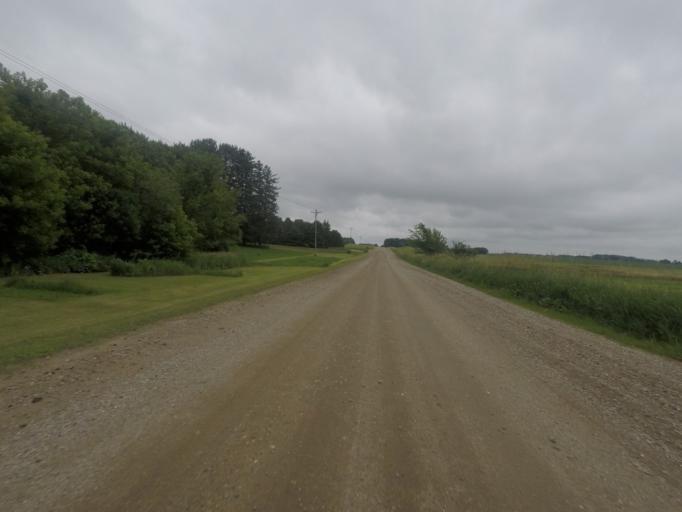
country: US
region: Minnesota
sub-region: Steele County
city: Owatonna
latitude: 44.0373
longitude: -93.0871
